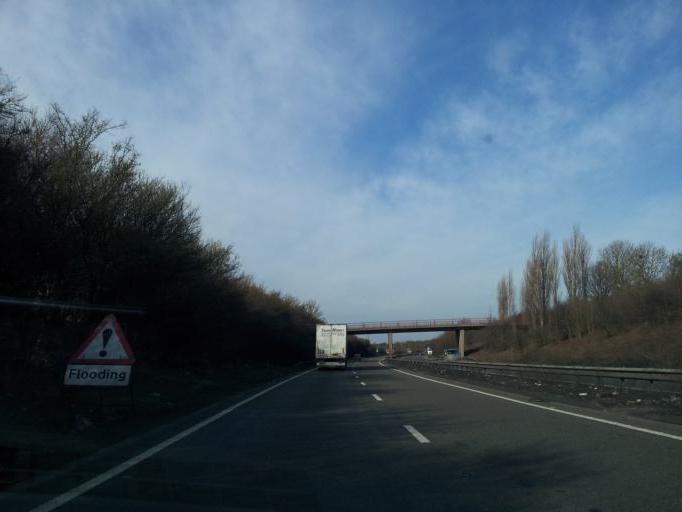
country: GB
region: England
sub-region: Nottinghamshire
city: Newark on Trent
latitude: 53.0416
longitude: -0.7781
